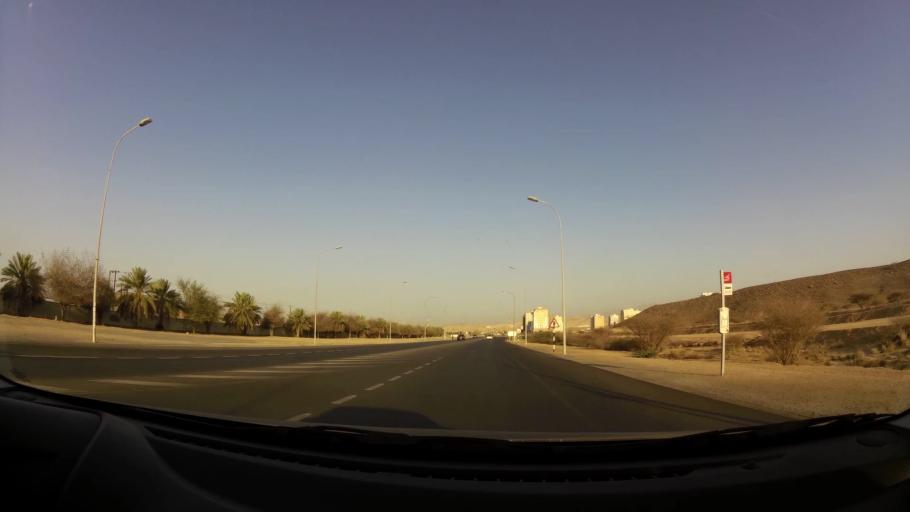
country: OM
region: Muhafazat Masqat
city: As Sib al Jadidah
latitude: 23.5803
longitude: 58.1754
